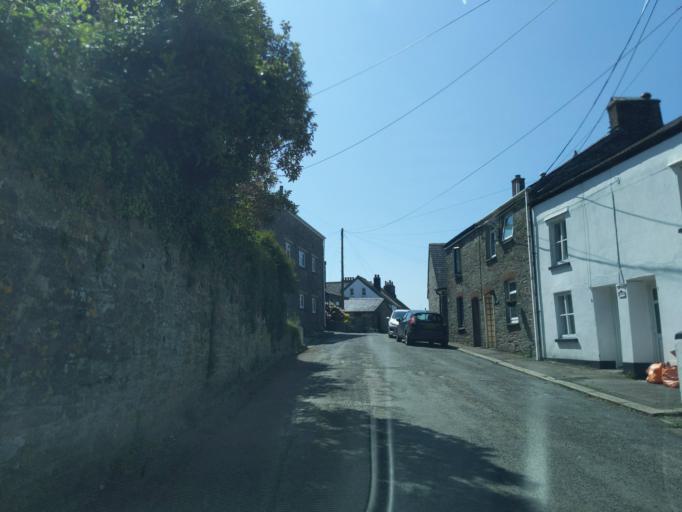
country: GB
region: England
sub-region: Cornwall
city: Pillaton
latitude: 50.4217
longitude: -4.2911
